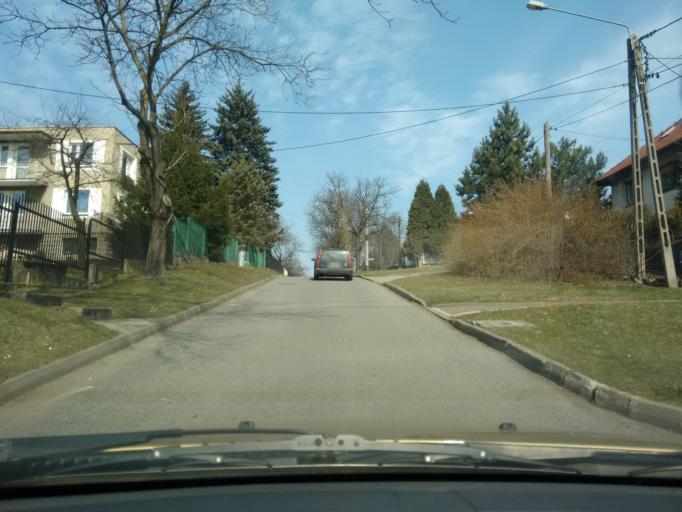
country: PL
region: Silesian Voivodeship
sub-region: Powiat cieszynski
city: Puncow
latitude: 49.7499
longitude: 18.6667
